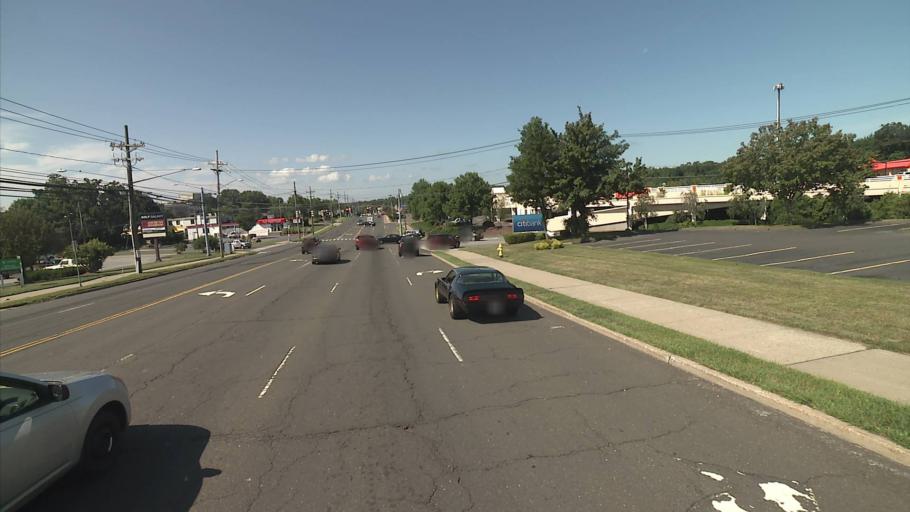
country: US
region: Connecticut
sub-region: Fairfield County
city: Darien
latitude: 41.0968
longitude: -73.4464
